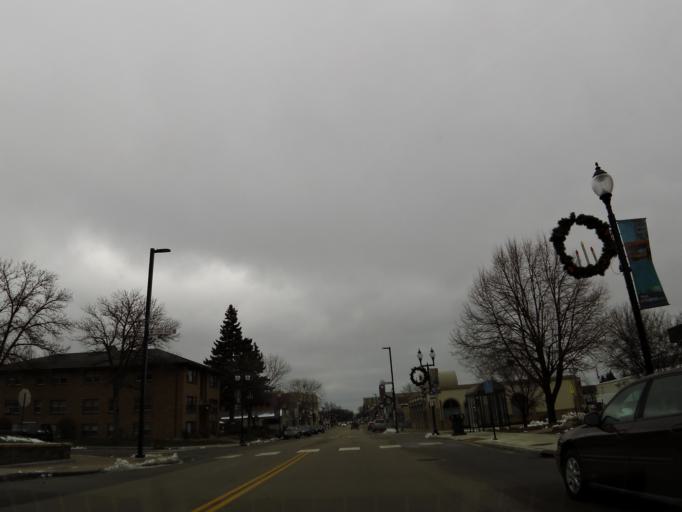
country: US
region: Minnesota
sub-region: Hennepin County
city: Minnetonka Mills
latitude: 44.9244
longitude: -93.4170
